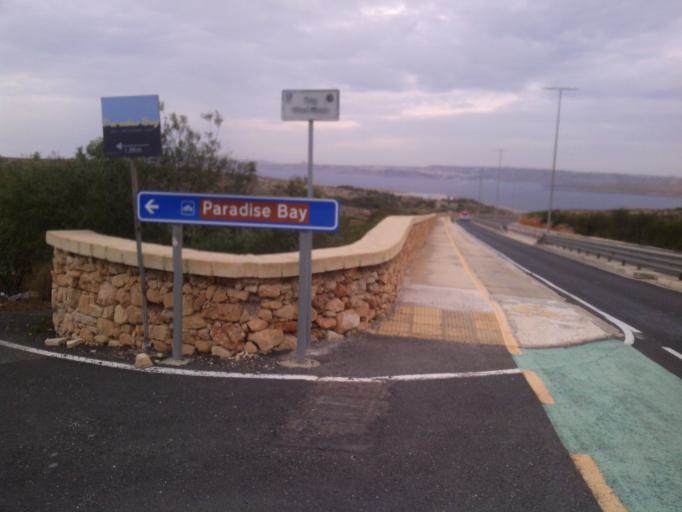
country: MT
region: Il-Mellieha
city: Mellieha
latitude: 35.9798
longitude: 14.3423
